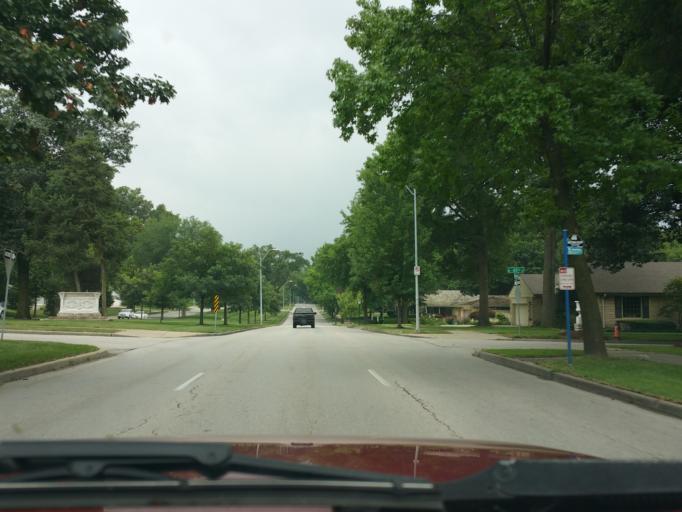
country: US
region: Kansas
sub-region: Johnson County
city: Mission Hills
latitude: 39.0109
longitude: -94.6026
